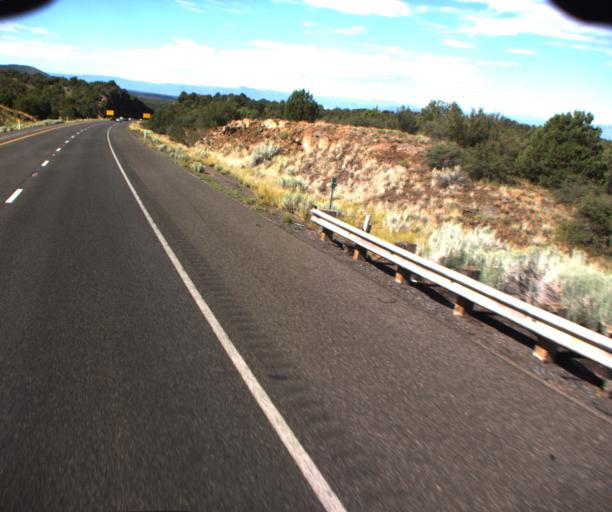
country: US
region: Arizona
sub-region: Yavapai County
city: Village of Oak Creek (Big Park)
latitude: 34.7942
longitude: -111.6008
